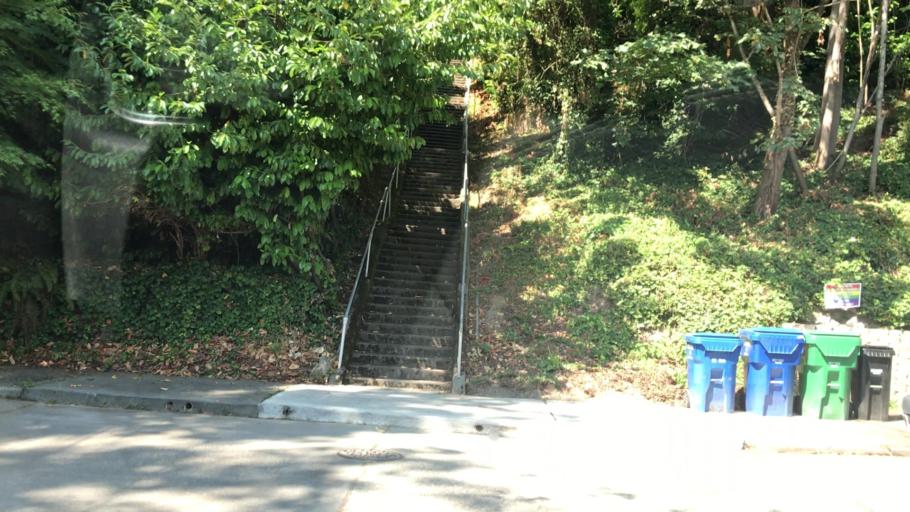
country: US
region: Washington
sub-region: King County
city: Seattle
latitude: 47.6009
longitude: -122.2919
